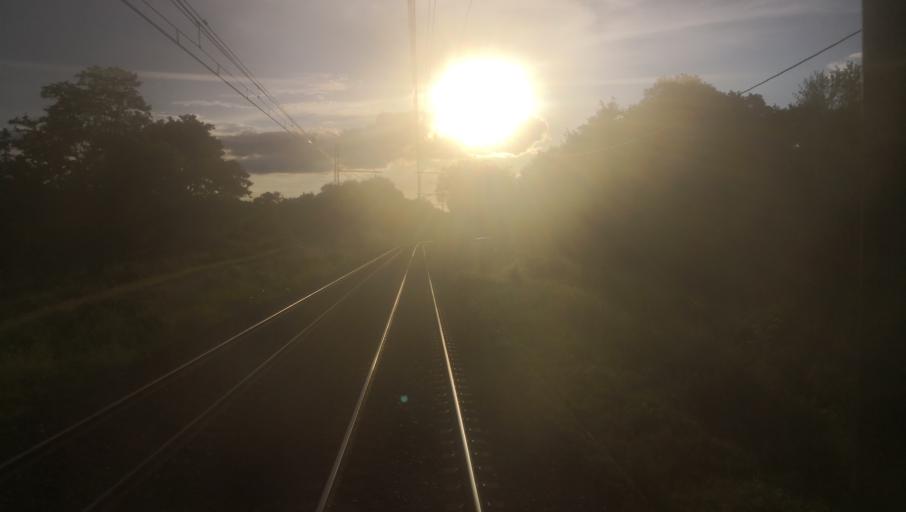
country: FR
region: Centre
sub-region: Departement de l'Indre
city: Le Pechereau
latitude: 46.4948
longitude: 1.5290
